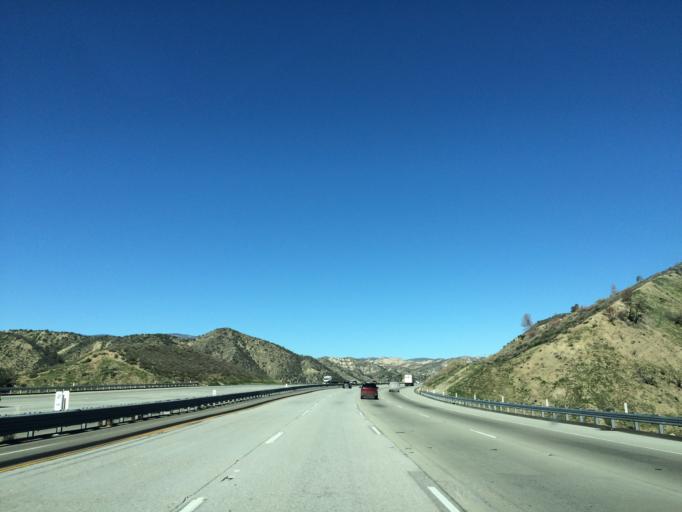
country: US
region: California
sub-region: Kern County
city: Lebec
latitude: 34.6876
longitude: -118.7861
